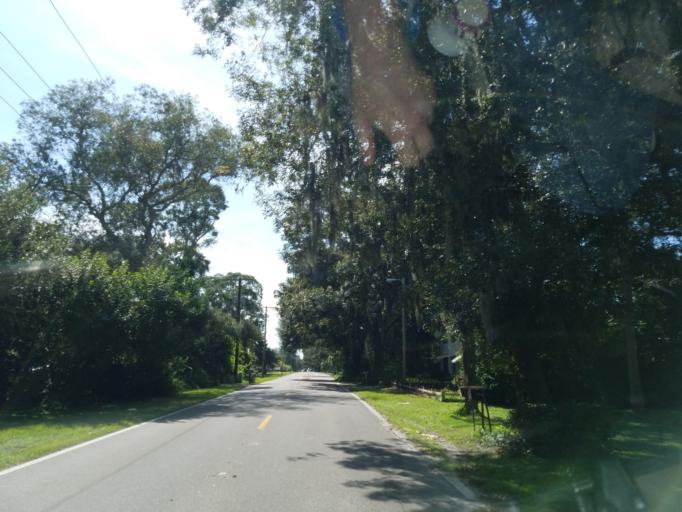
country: US
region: Florida
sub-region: Hillsborough County
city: Riverview
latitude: 27.8790
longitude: -82.3217
